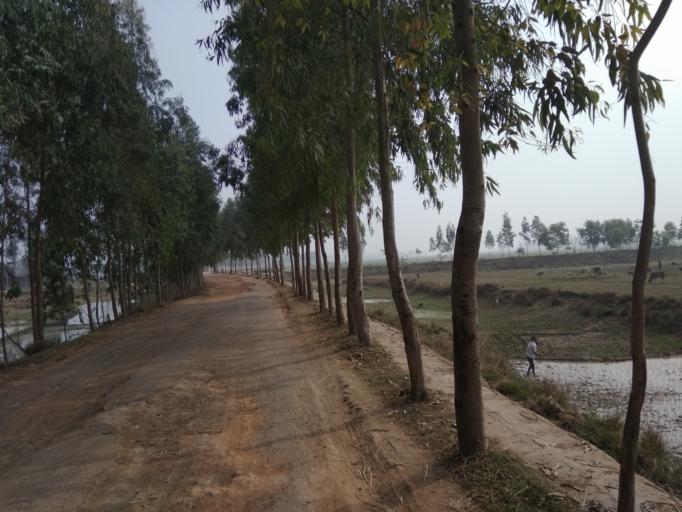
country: BD
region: Rajshahi
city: Bogra
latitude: 24.4762
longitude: 89.2687
